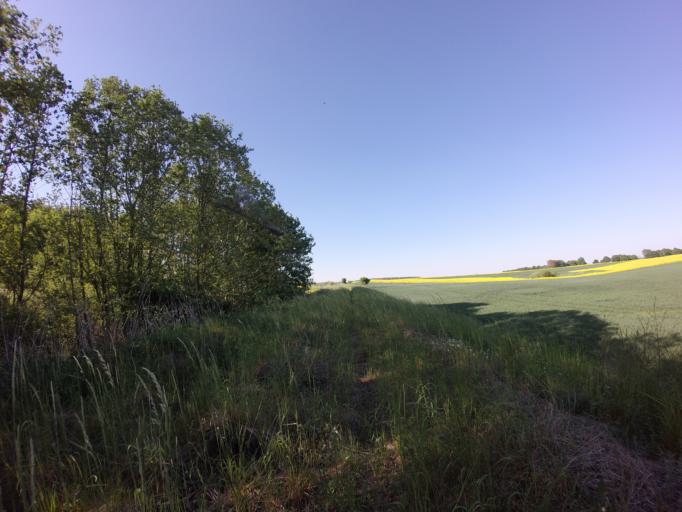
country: PL
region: West Pomeranian Voivodeship
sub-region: Powiat choszczenski
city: Choszczno
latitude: 53.1452
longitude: 15.3711
